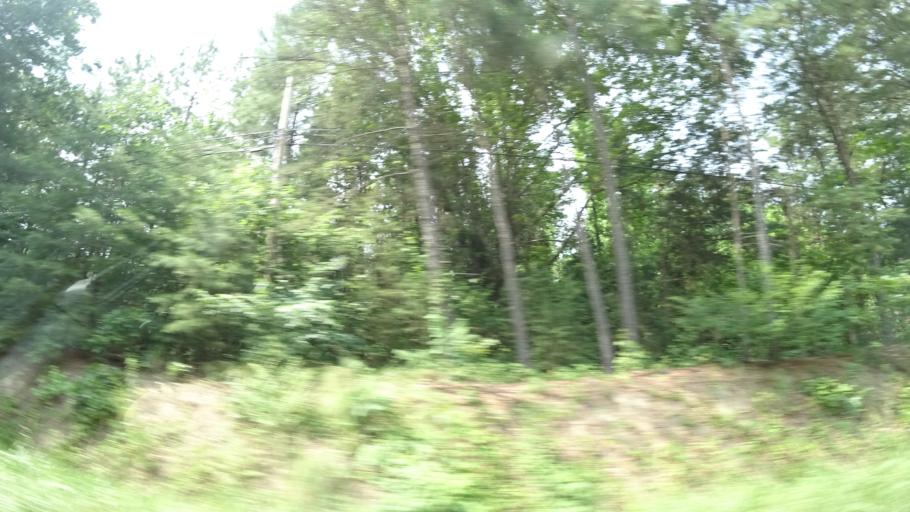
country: US
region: Virginia
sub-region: Spotsylvania County
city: Spotsylvania Courthouse
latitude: 38.1399
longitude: -77.5584
